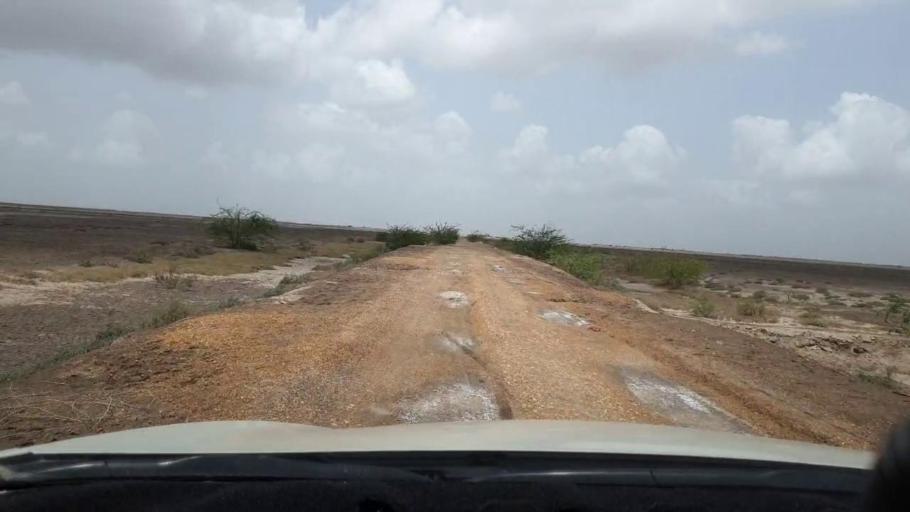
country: PK
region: Sindh
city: Kadhan
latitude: 24.3603
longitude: 68.8371
